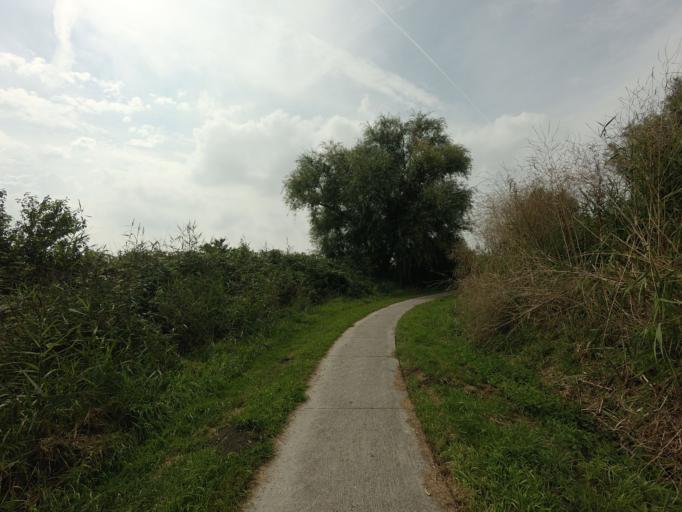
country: NL
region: Flevoland
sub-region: Gemeente Almere
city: Almere Stad
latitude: 52.3998
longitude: 5.2084
